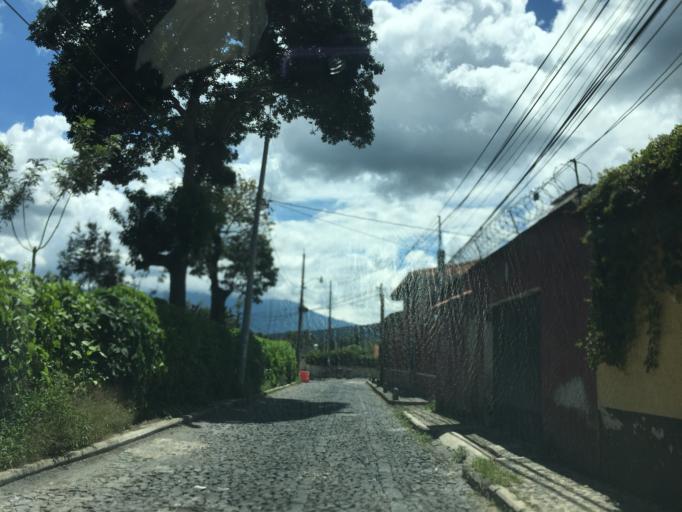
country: GT
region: Sacatepequez
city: Antigua Guatemala
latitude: 14.5456
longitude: -90.7312
